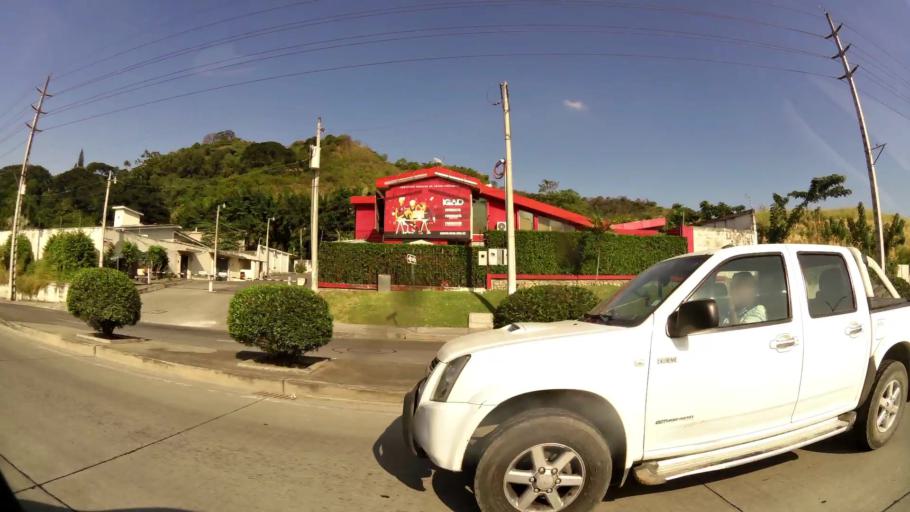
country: EC
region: Guayas
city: Guayaquil
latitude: -2.1655
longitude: -79.9337
